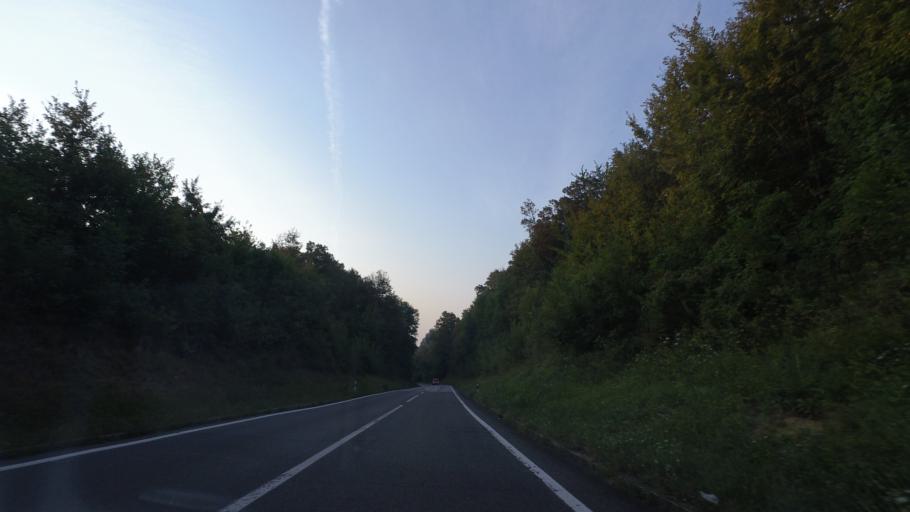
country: HR
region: Brodsko-Posavska
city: Cernik
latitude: 45.2851
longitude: 17.4127
